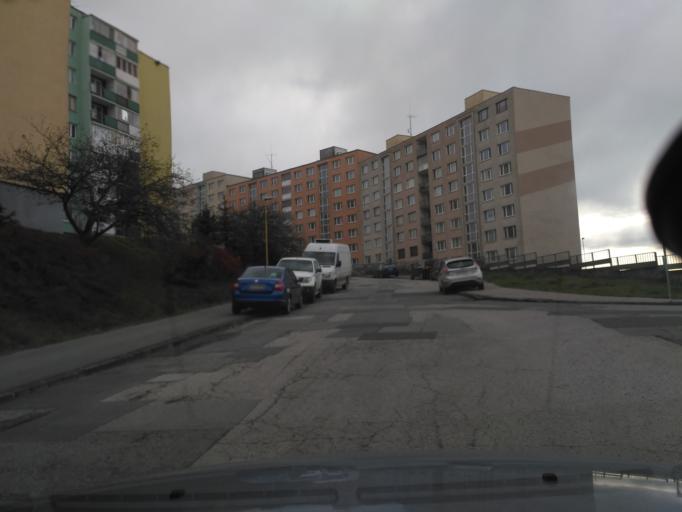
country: SK
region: Kosicky
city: Kosice
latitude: 48.7320
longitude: 21.2817
